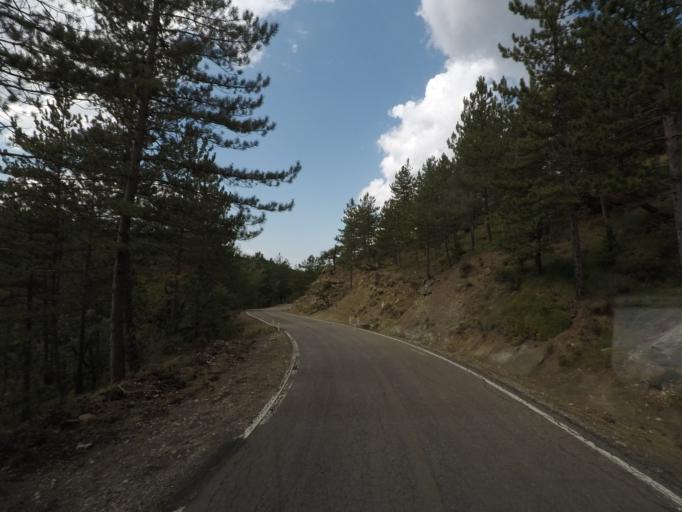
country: ES
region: Aragon
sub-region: Provincia de Huesca
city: Fiscal
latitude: 42.4068
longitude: -0.1461
